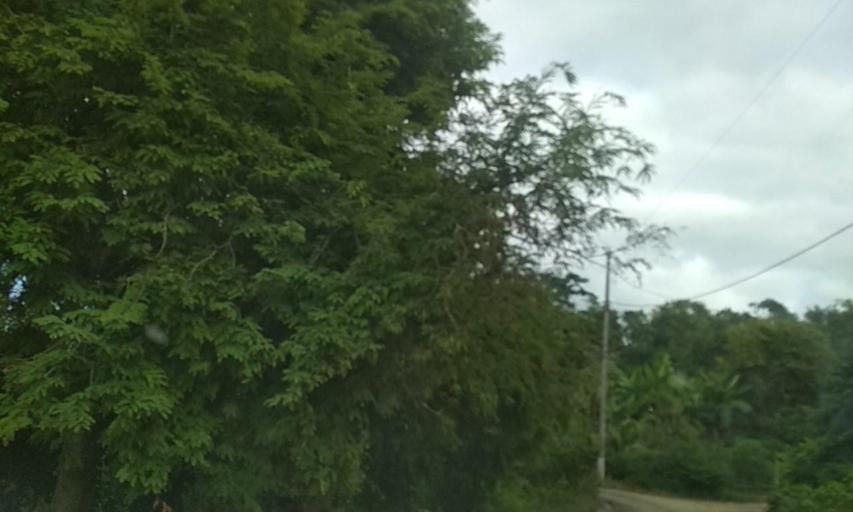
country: MX
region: Veracruz
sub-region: Papantla
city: Polutla
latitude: 20.5749
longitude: -97.2518
